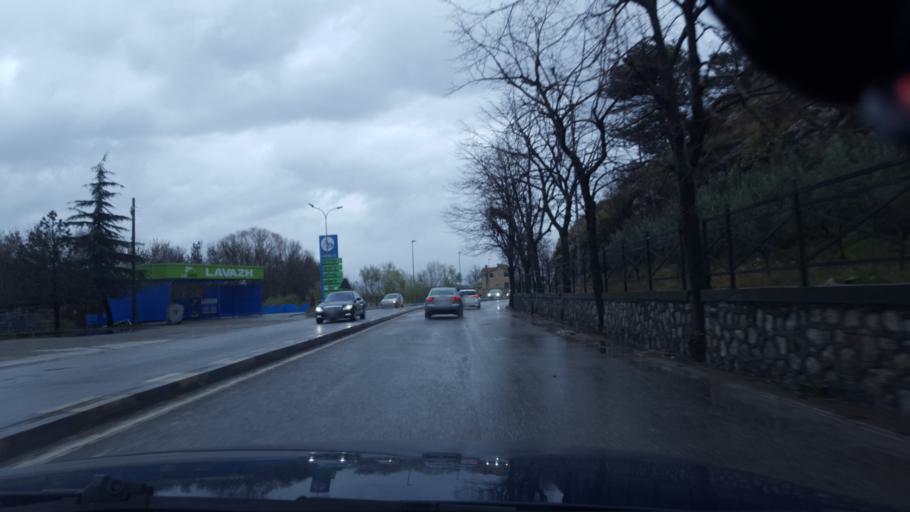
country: AL
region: Shkoder
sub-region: Rrethi i Shkodres
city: Berdica e Madhe
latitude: 42.0457
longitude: 19.4902
